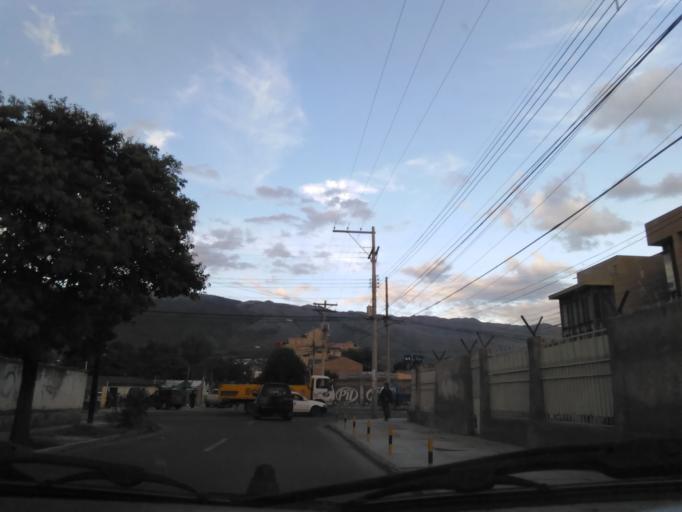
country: BO
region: Cochabamba
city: Cochabamba
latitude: -17.3833
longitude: -66.1653
